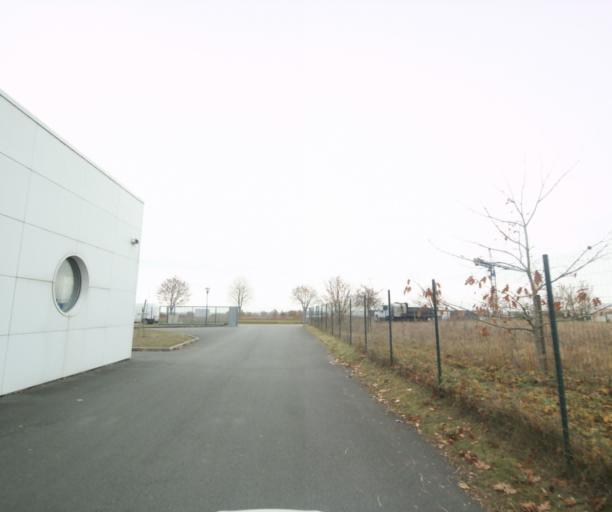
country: FR
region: Poitou-Charentes
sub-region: Departement de la Charente-Maritime
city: Saintes
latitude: 45.7197
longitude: -0.6486
